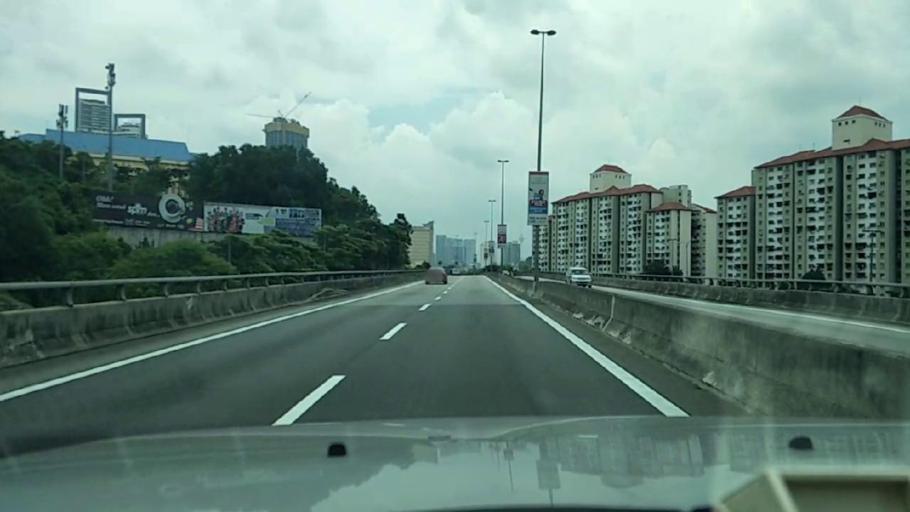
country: MY
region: Kuala Lumpur
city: Kuala Lumpur
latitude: 3.1070
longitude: 101.6731
